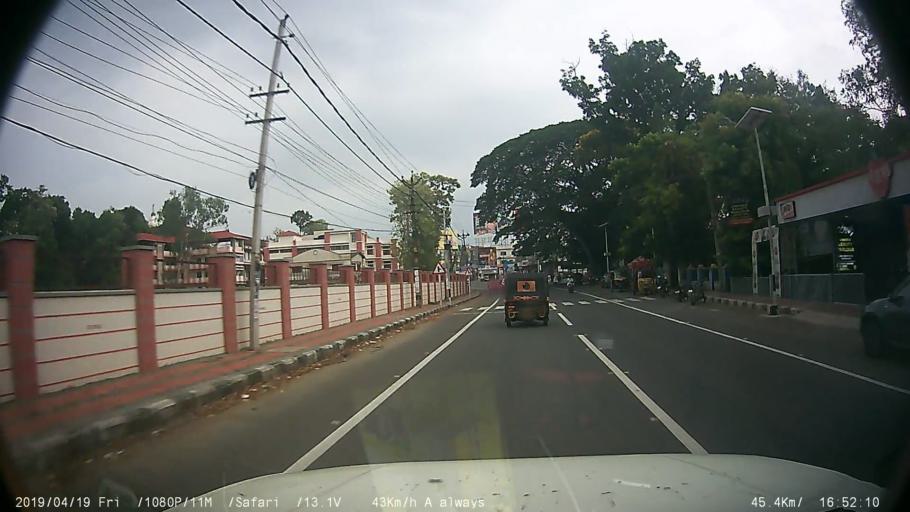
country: IN
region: Kerala
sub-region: Kottayam
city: Changanacheri
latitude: 9.4526
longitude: 76.5369
